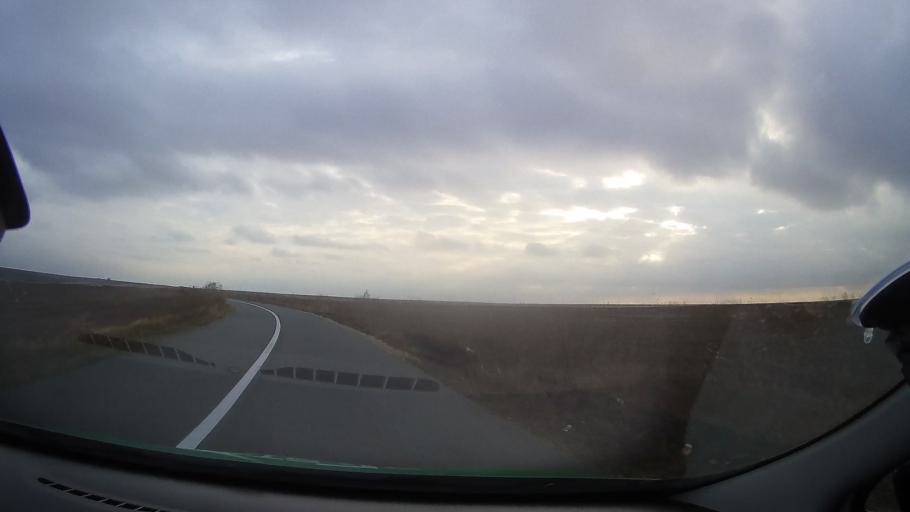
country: RO
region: Constanta
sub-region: Comuna Pestera
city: Pestera
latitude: 44.1515
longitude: 28.1138
